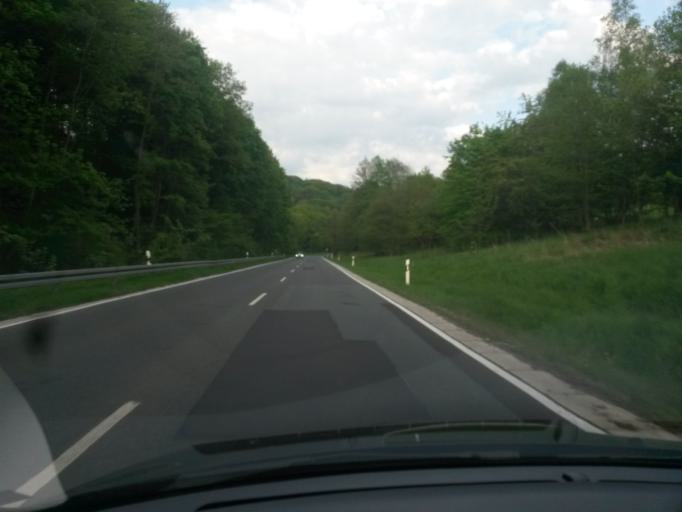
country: DE
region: Hesse
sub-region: Regierungsbezirk Kassel
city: Baunatal
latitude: 51.3093
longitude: 9.3842
